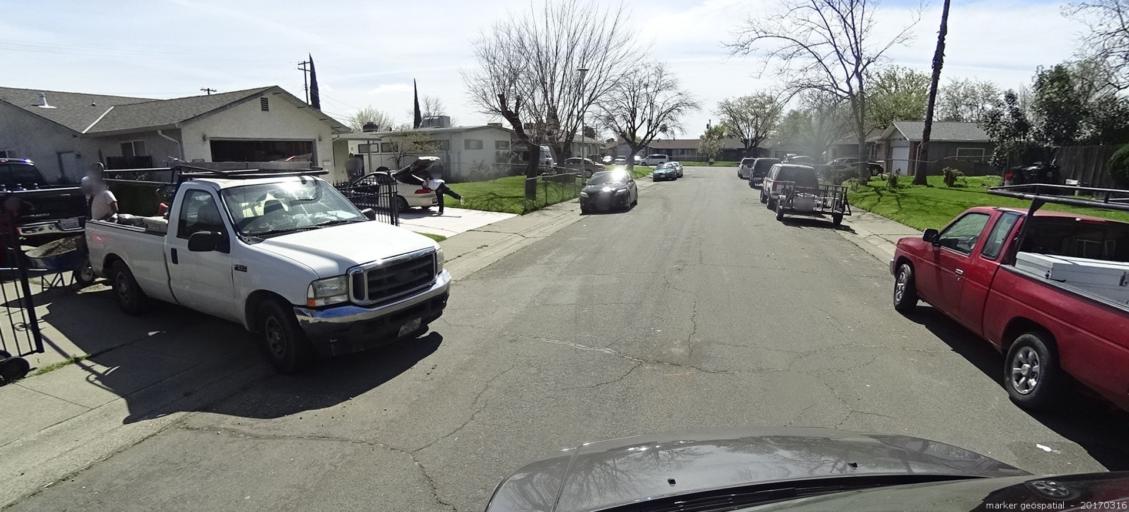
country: US
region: California
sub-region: Sacramento County
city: Parkway
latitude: 38.4789
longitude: -121.4832
